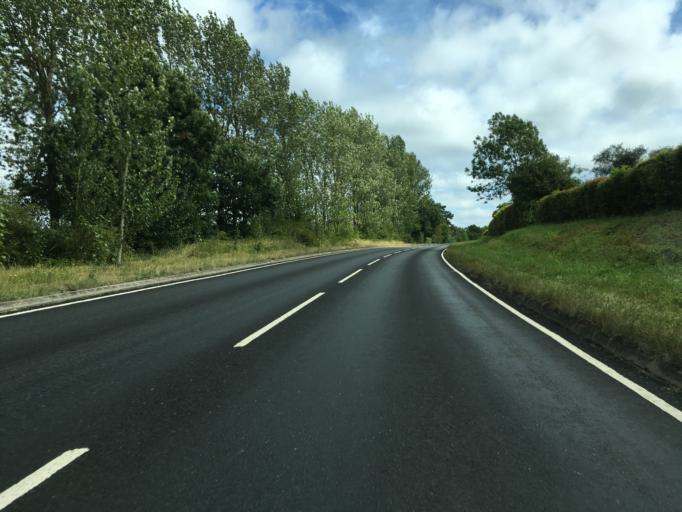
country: GB
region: England
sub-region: Kent
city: Cranbrook
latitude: 51.1109
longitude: 0.5388
